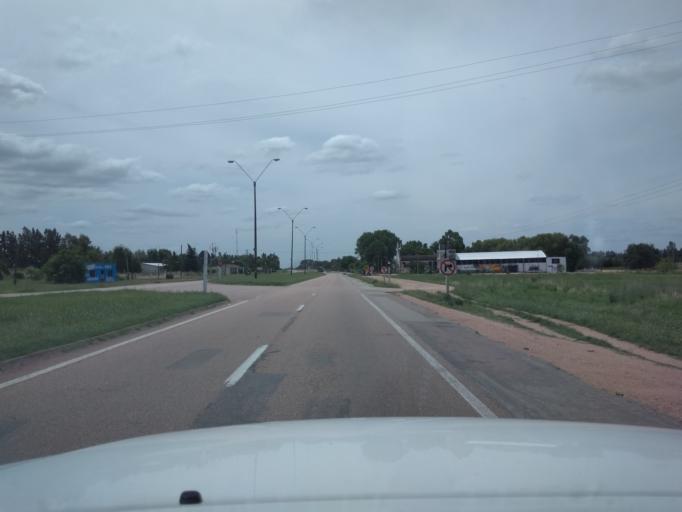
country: UY
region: Canelones
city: Joanico
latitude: -34.5959
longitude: -56.2620
